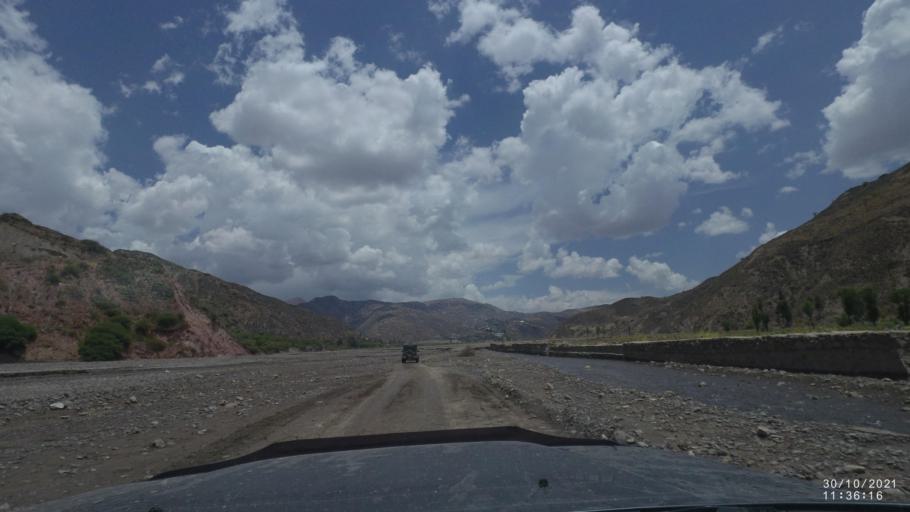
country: BO
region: Cochabamba
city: Sipe Sipe
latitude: -17.5234
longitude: -66.6026
